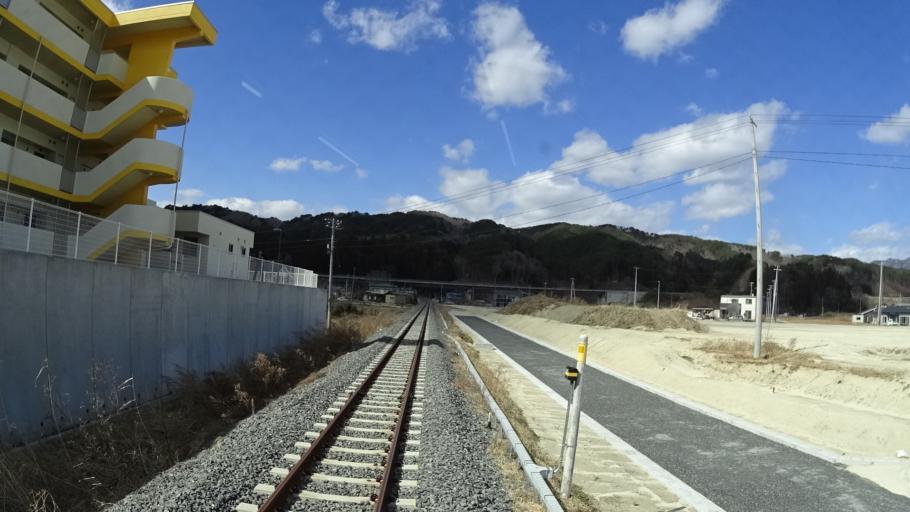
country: JP
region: Iwate
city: Yamada
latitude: 39.4747
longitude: 141.9468
